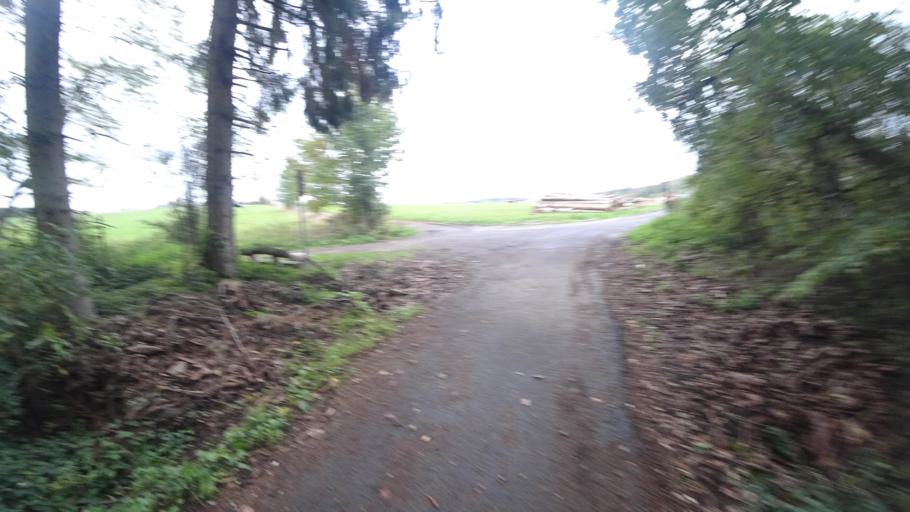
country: DE
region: Rheinland-Pfalz
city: Nordhofen
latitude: 50.5252
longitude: 7.7379
